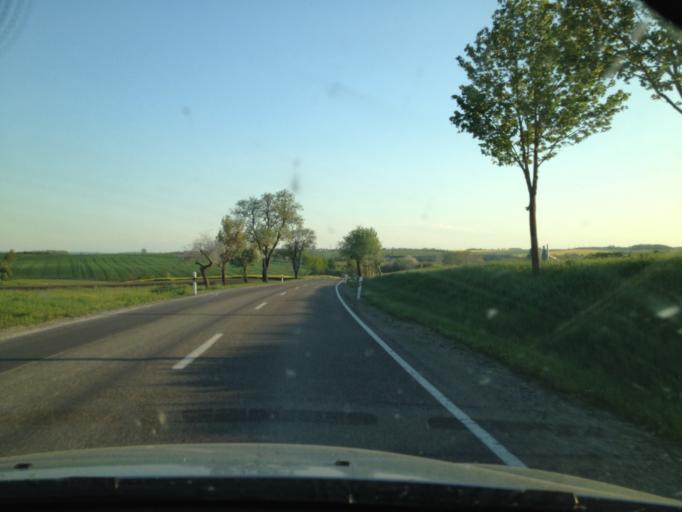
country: DE
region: Bavaria
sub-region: Regierungsbezirk Mittelfranken
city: Steinsfeld
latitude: 49.4160
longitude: 10.2113
